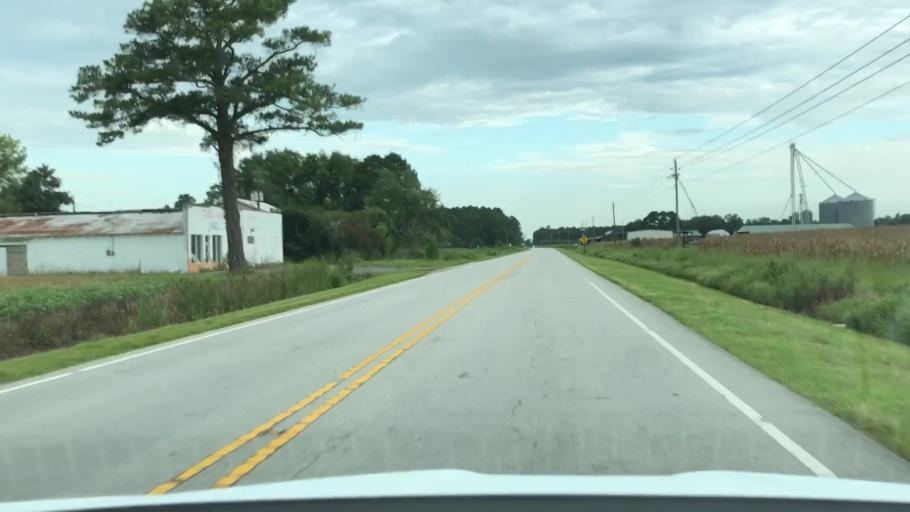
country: US
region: North Carolina
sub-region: Jones County
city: Trenton
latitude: 35.0688
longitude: -77.3688
